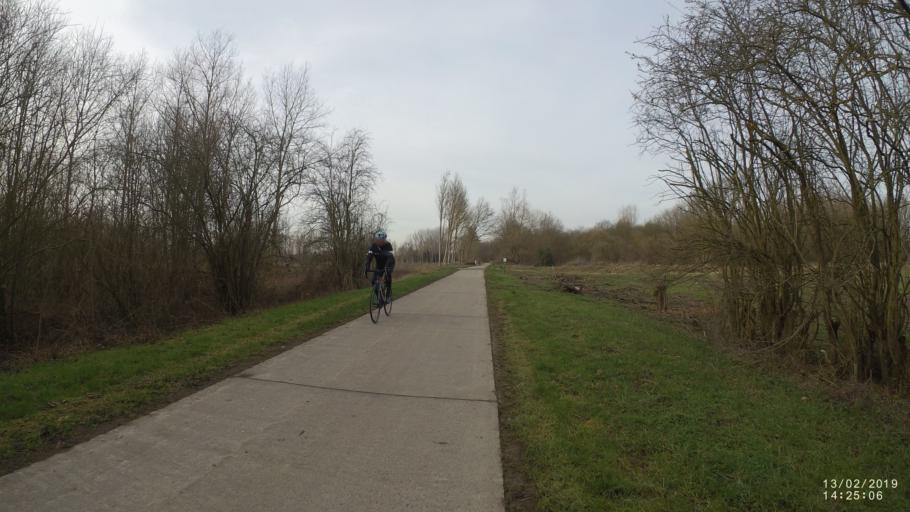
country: BE
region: Flanders
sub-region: Provincie Vlaams-Brabant
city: Zoutleeuw
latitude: 50.8428
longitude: 5.0678
